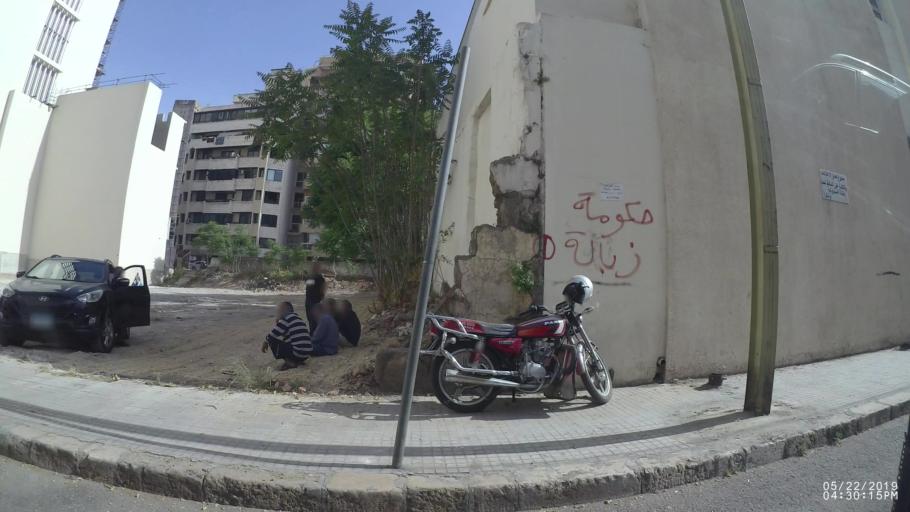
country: LB
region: Beyrouth
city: Beirut
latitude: 33.8975
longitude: 35.4946
